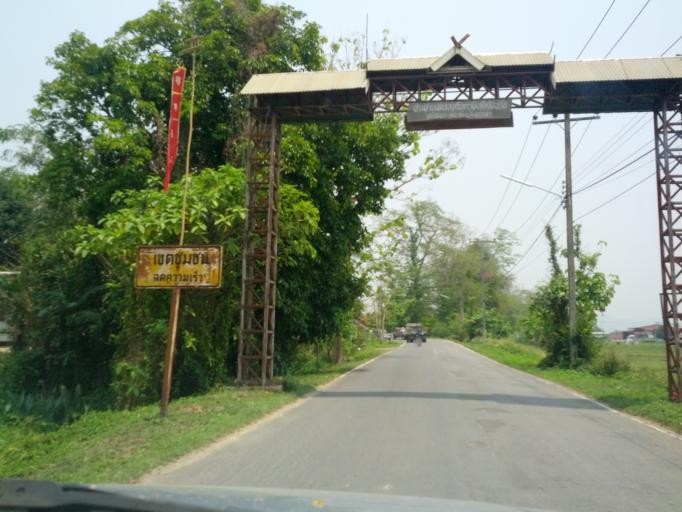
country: TH
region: Chiang Mai
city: San Sai
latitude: 18.8912
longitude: 99.0823
